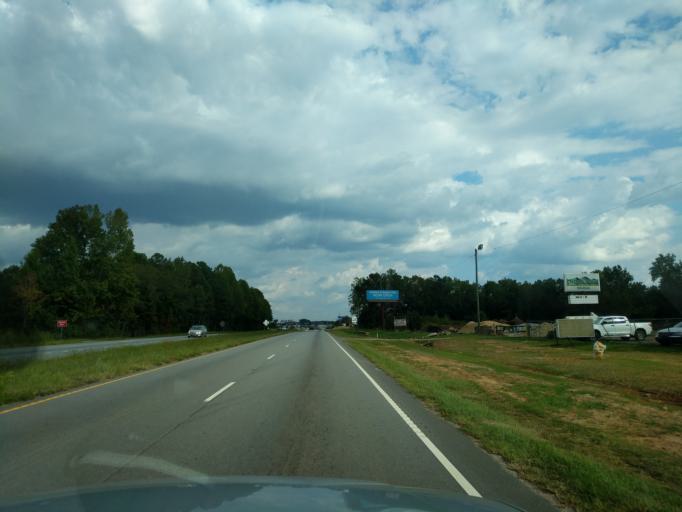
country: US
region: South Carolina
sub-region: Anderson County
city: Powdersville
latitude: 34.7915
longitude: -82.4926
